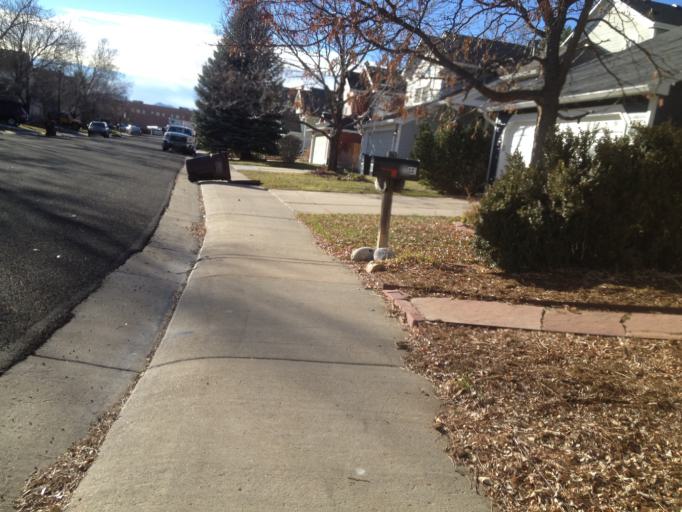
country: US
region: Colorado
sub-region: Boulder County
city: Louisville
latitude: 39.9761
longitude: -105.1545
